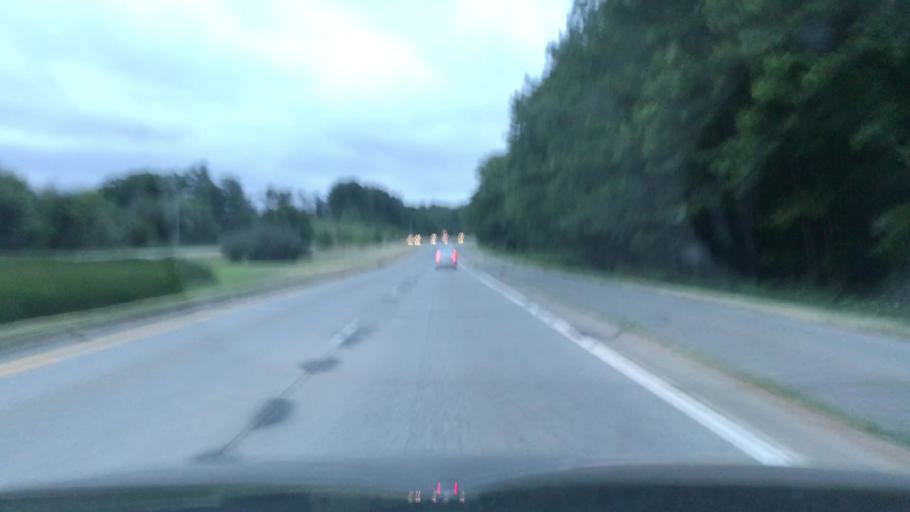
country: US
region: Michigan
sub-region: Kent County
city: East Grand Rapids
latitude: 42.9488
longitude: -85.5866
